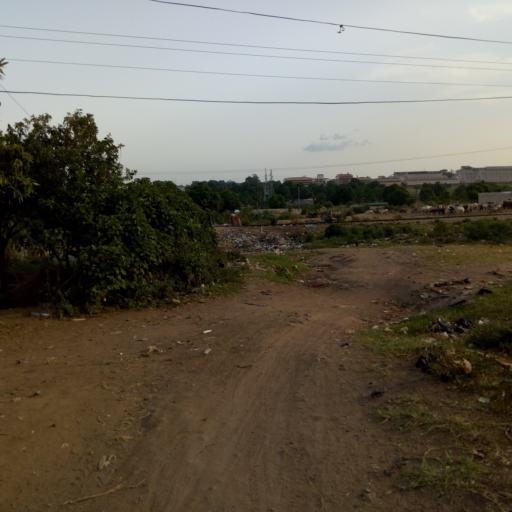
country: CI
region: Vallee du Bandama
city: Bouake
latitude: 7.6998
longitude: -5.0447
